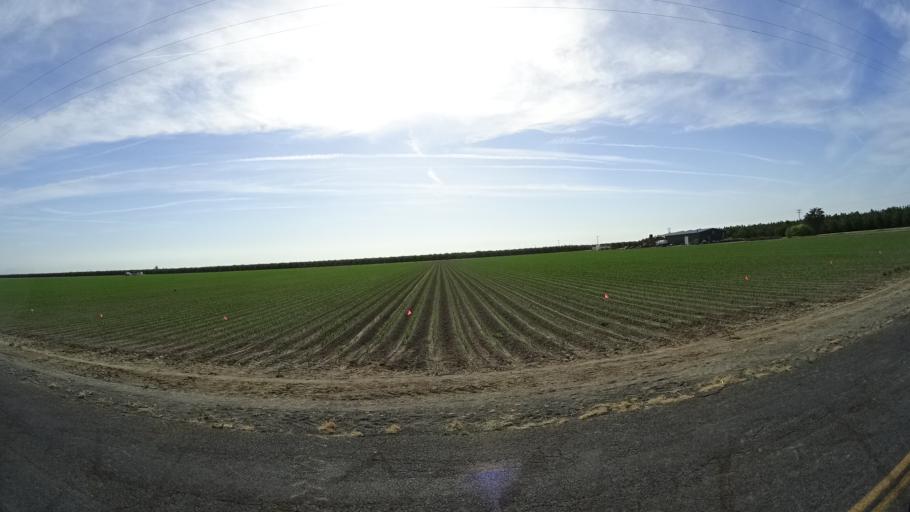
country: US
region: California
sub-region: Kings County
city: Hanford
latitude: 36.3880
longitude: -119.5471
